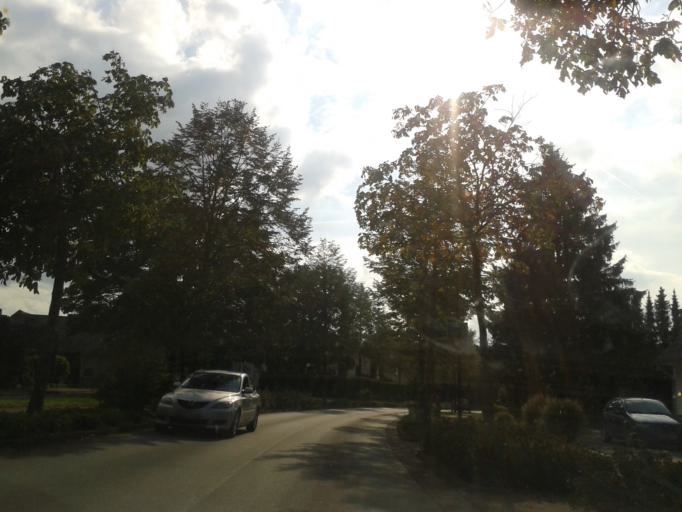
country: DE
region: North Rhine-Westphalia
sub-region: Regierungsbezirk Detmold
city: Schlangen
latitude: 51.8121
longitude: 8.8474
